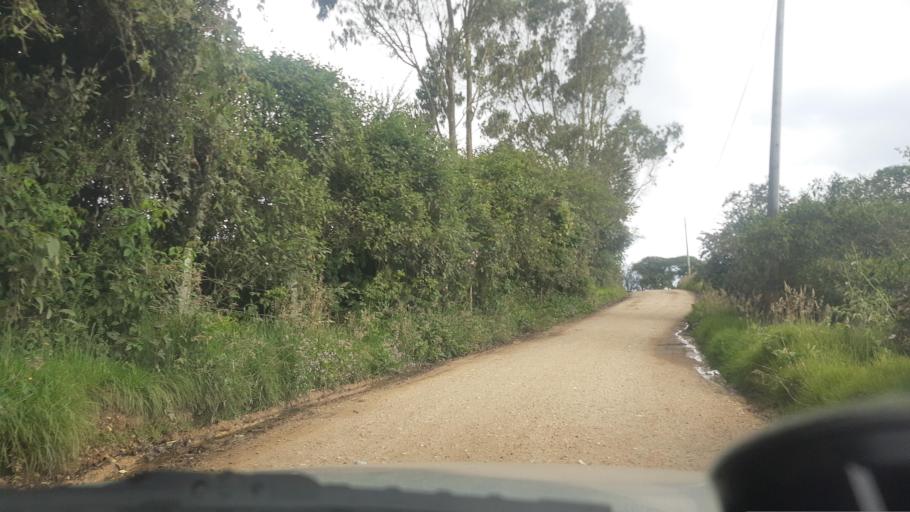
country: CO
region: Cundinamarca
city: Suesca
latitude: 5.1353
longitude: -73.7822
